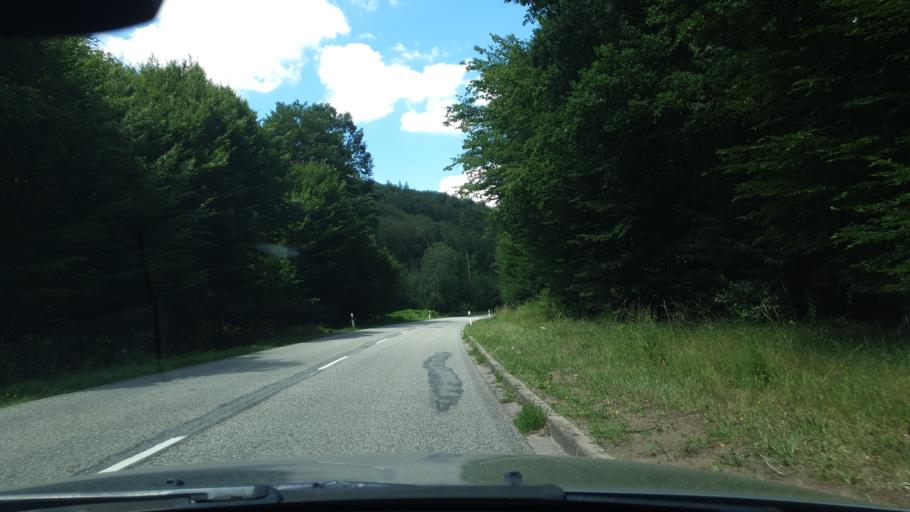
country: DE
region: Rheinland-Pfalz
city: Stelzenberg
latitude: 49.4000
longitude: 7.7445
